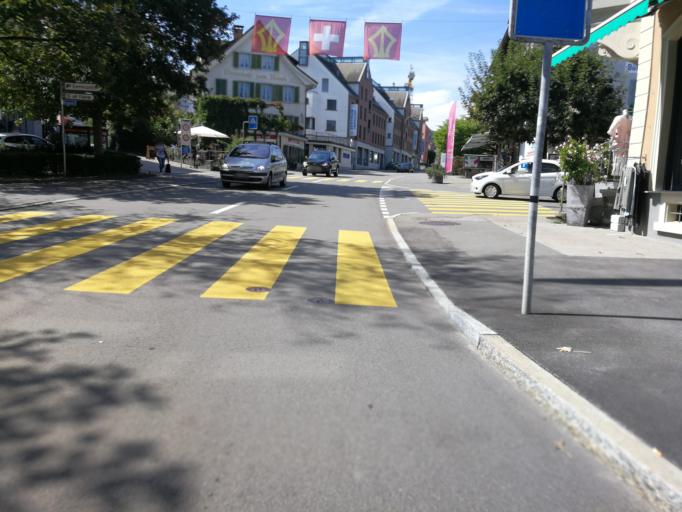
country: CH
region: Zurich
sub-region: Bezirk Horgen
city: Waedenswil / Dorf (Waedenswil)
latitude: 47.2298
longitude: 8.6701
